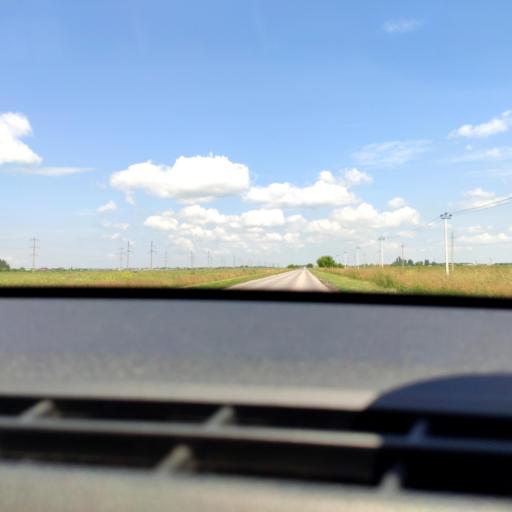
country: RU
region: Samara
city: Podstepki
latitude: 53.5478
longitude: 49.0891
